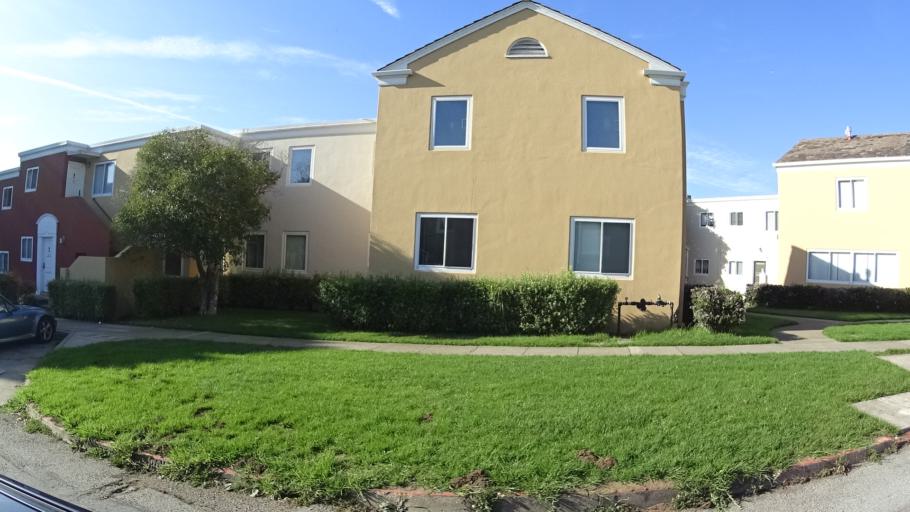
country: US
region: California
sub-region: San Mateo County
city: Daly City
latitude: 37.7201
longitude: -122.4791
